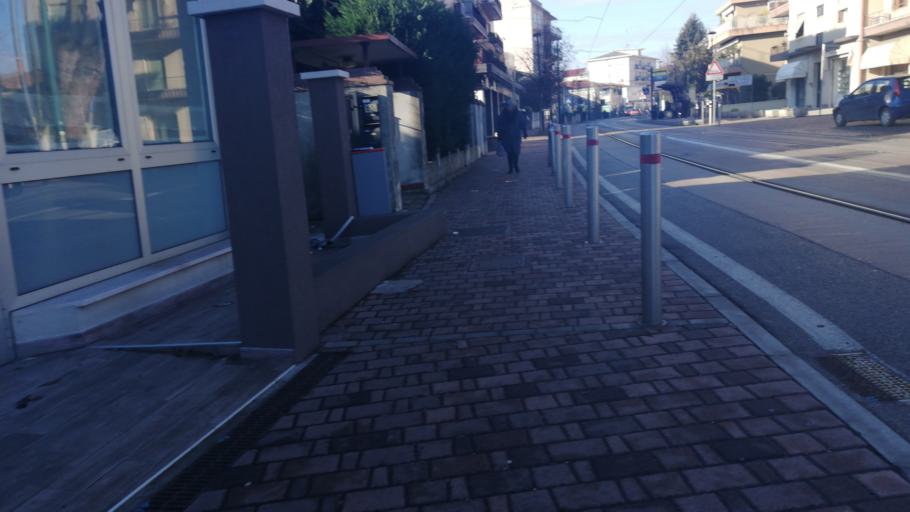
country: IT
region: Veneto
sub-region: Provincia di Venezia
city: Campalto
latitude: 45.5037
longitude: 12.2589
